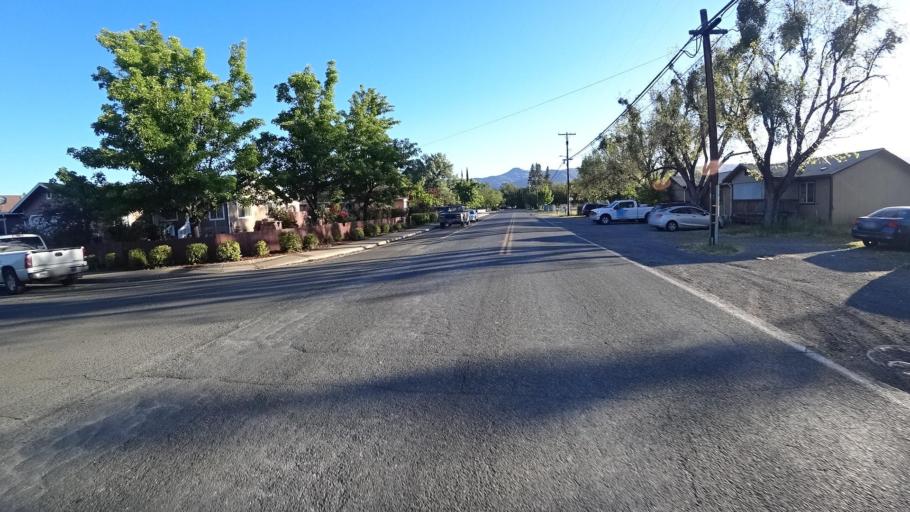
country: US
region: California
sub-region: Lake County
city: Upper Lake
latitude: 39.1626
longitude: -122.9048
